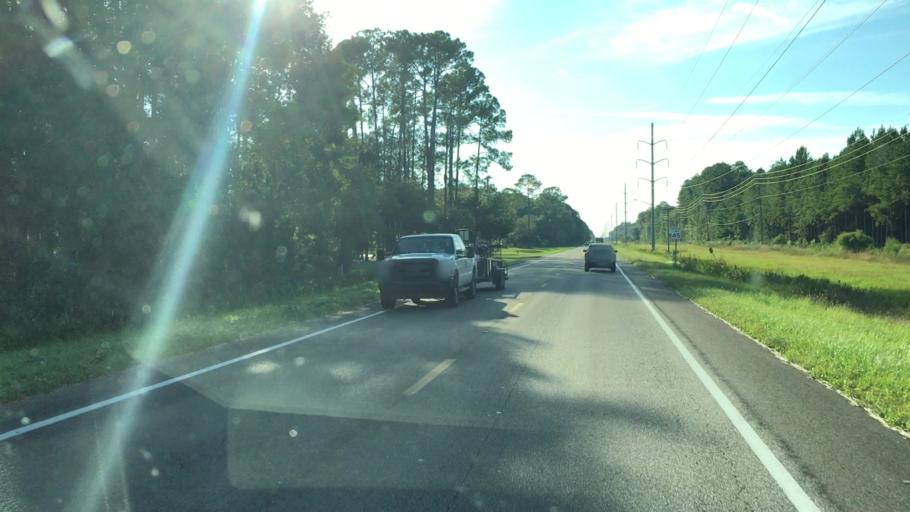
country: US
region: Florida
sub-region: Alachua County
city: Gainesville
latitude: 29.7032
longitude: -82.3288
